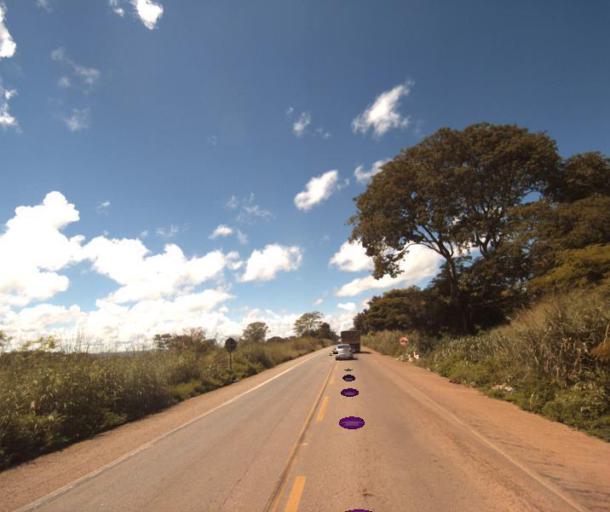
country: BR
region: Goias
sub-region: Pirenopolis
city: Pirenopolis
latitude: -16.0213
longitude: -49.1071
